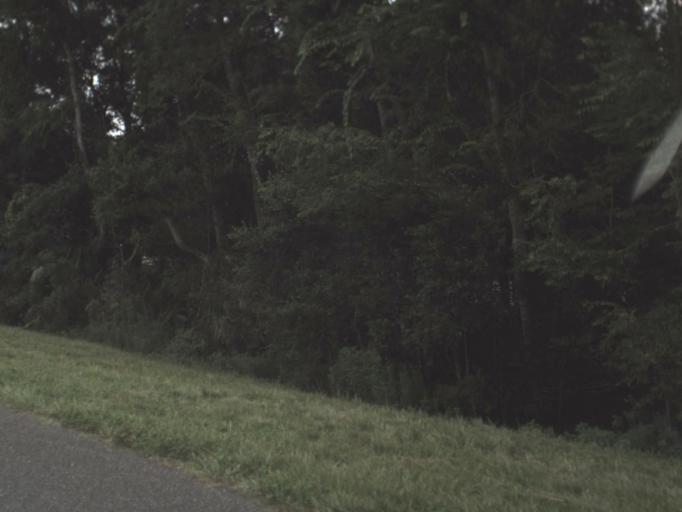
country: US
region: Florida
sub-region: Citrus County
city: Inverness
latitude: 28.8506
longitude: -82.2438
